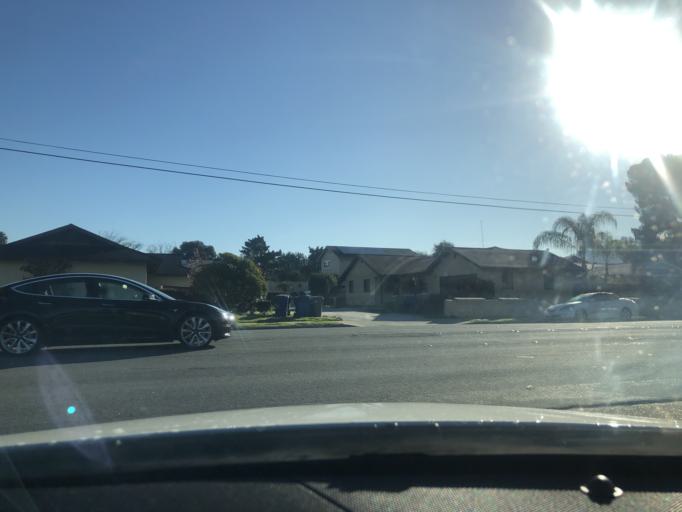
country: US
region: California
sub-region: San Diego County
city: El Cajon
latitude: 32.7827
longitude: -116.9580
